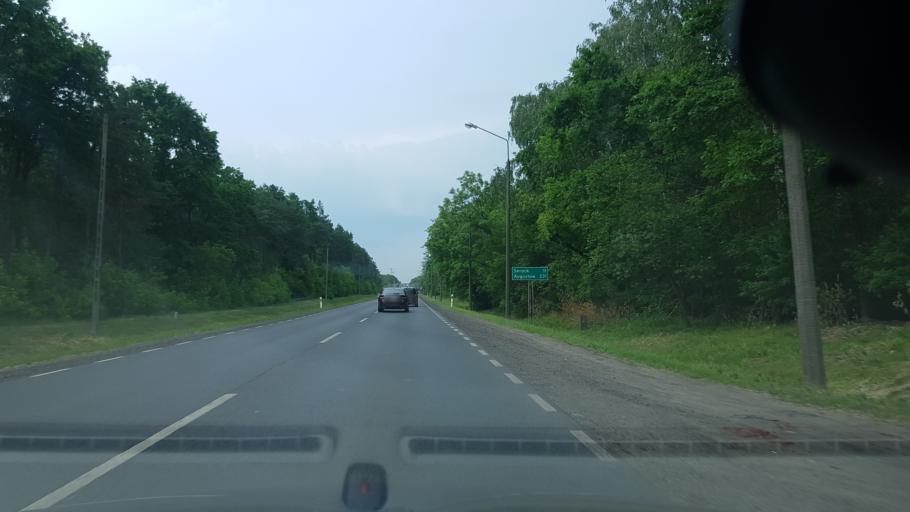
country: PL
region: Masovian Voivodeship
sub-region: Powiat legionowski
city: Michalow-Reginow
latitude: 52.4316
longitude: 20.9845
